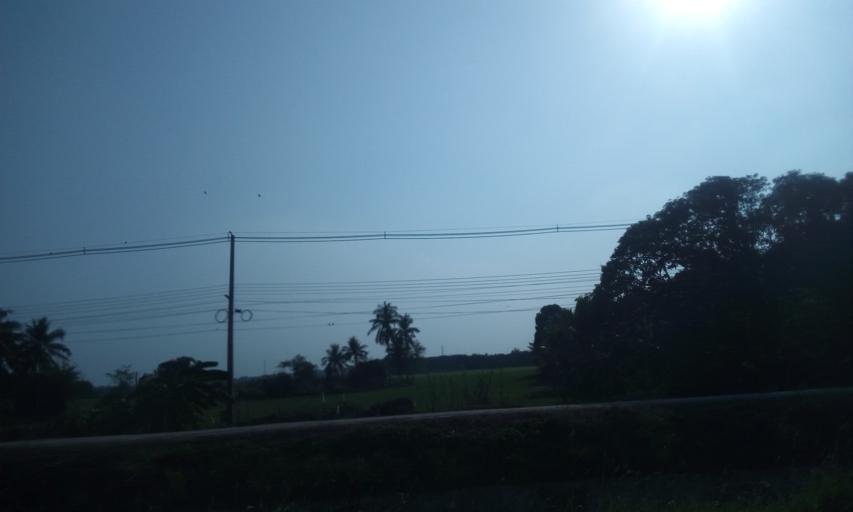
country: TH
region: Sing Buri
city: Sing Buri
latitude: 14.8489
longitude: 100.4171
